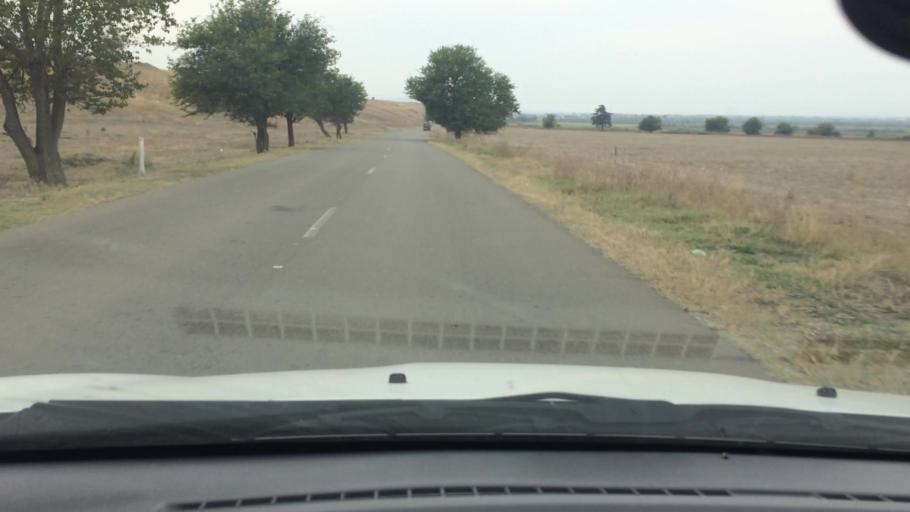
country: AM
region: Tavush
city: Berdavan
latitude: 41.3376
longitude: 45.0099
